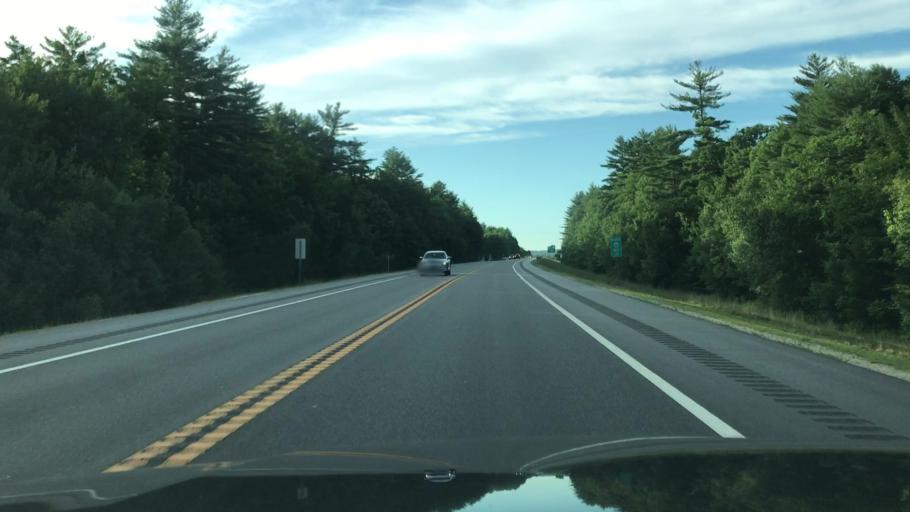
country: US
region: New Hampshire
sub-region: Strafford County
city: Farmington
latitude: 43.3818
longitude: -70.9964
